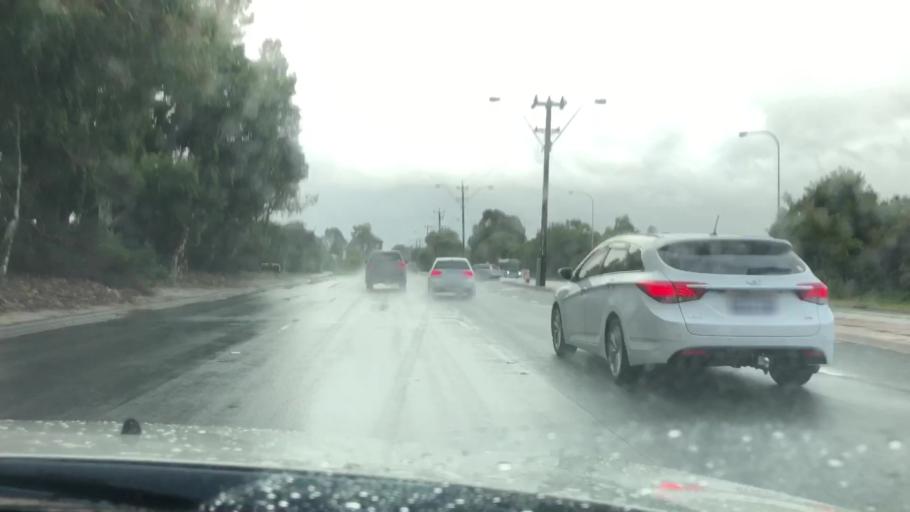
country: AU
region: Western Australia
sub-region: Canning
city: Rossmoyne
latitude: -32.0657
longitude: 115.8603
